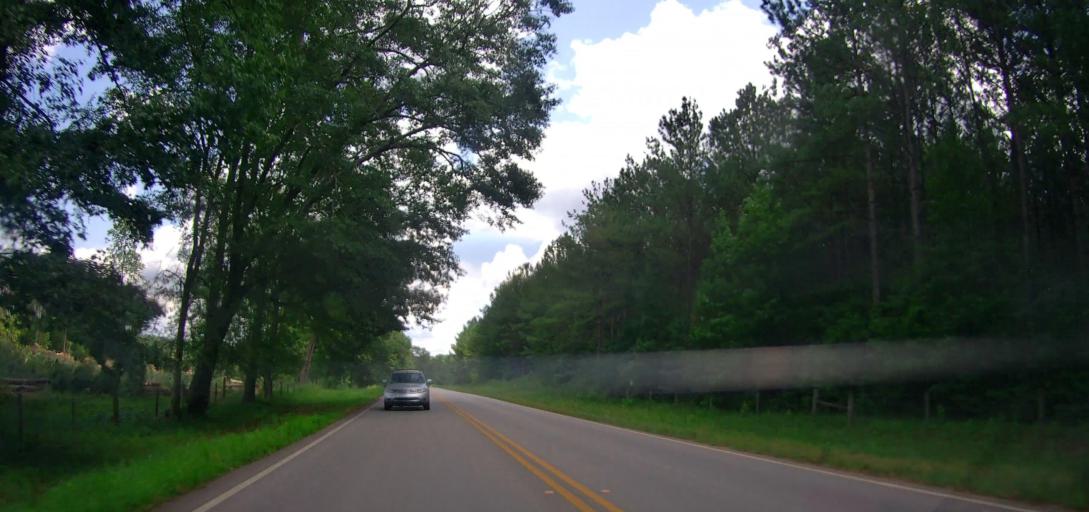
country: US
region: Georgia
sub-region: Troup County
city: Hogansville
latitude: 33.1489
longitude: -84.8493
